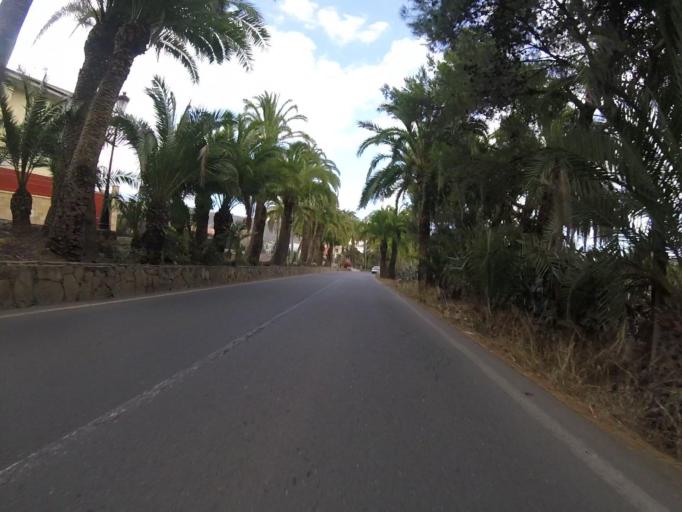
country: ES
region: Canary Islands
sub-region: Provincia de Las Palmas
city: Santa Brigida
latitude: 28.0364
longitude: -15.4955
